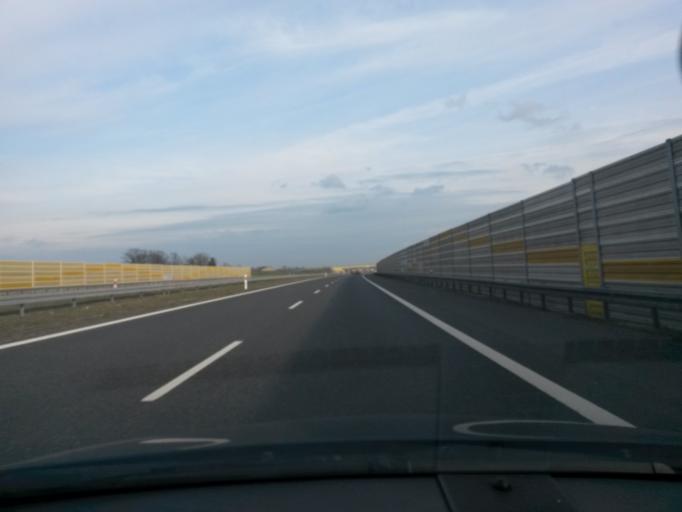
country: PL
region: Lodz Voivodeship
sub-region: Powiat poddebicki
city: Wartkowice
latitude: 51.9904
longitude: 19.0530
